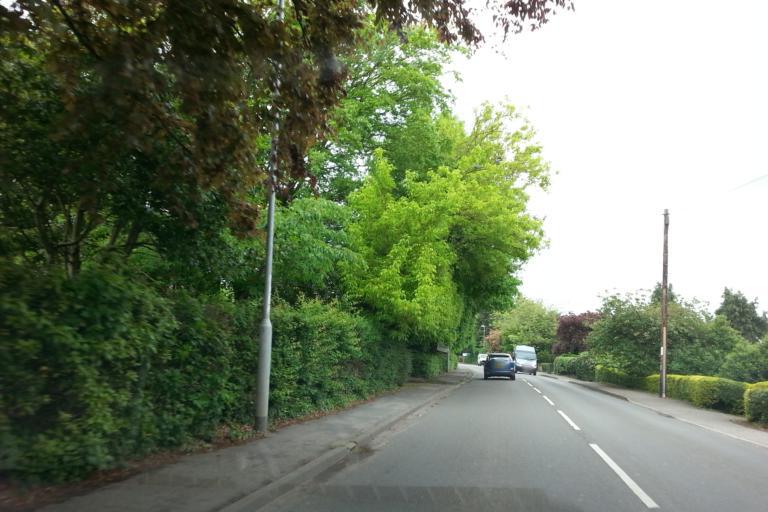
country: GB
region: England
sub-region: Cambridgeshire
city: Ramsey
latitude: 52.4428
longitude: -0.1131
